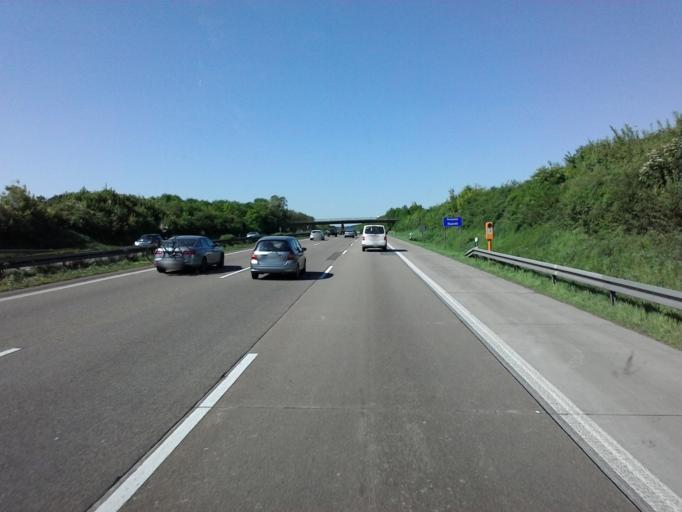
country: DE
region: North Rhine-Westphalia
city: Leichlingen
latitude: 51.0848
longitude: 6.9887
